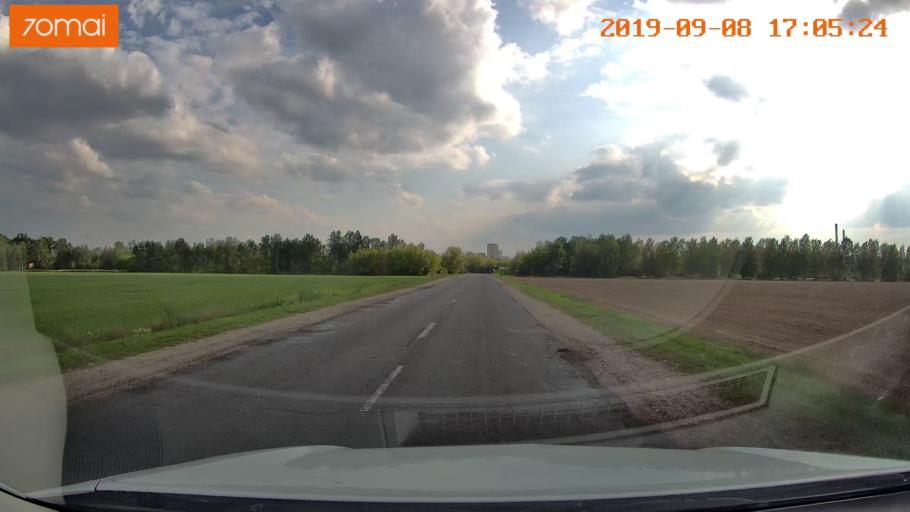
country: BY
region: Grodnenskaya
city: Hrodna
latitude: 53.6780
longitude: 23.9545
